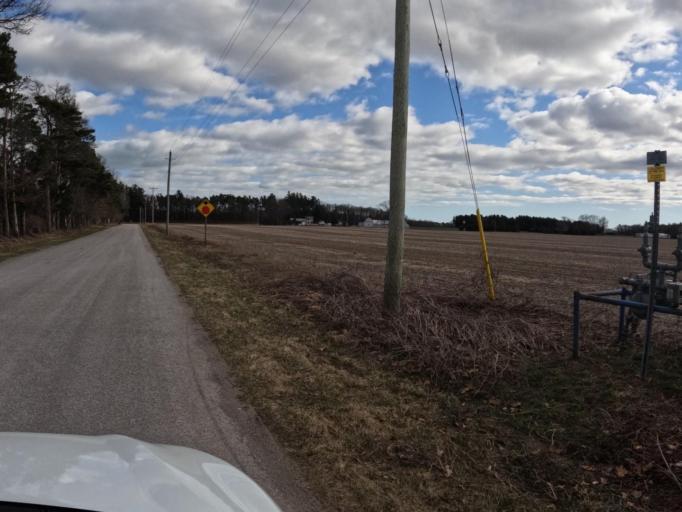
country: CA
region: Ontario
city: Norfolk County
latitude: 42.7425
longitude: -80.3799
